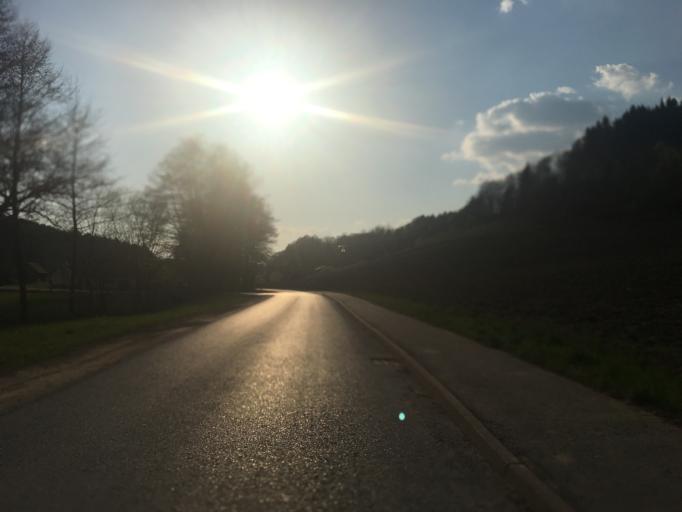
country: AT
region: Styria
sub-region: Politischer Bezirk Graz-Umgebung
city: Nestelbach bei Graz
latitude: 47.0837
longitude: 15.6168
